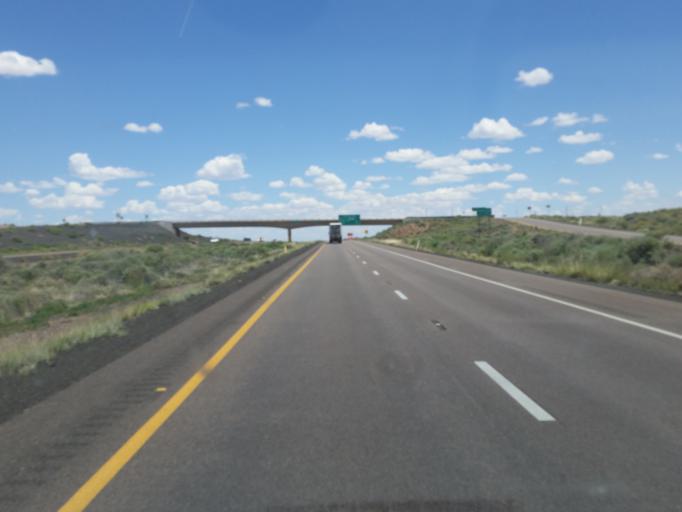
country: US
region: Arizona
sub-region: Navajo County
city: Holbrook
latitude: 34.9076
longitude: -110.2153
